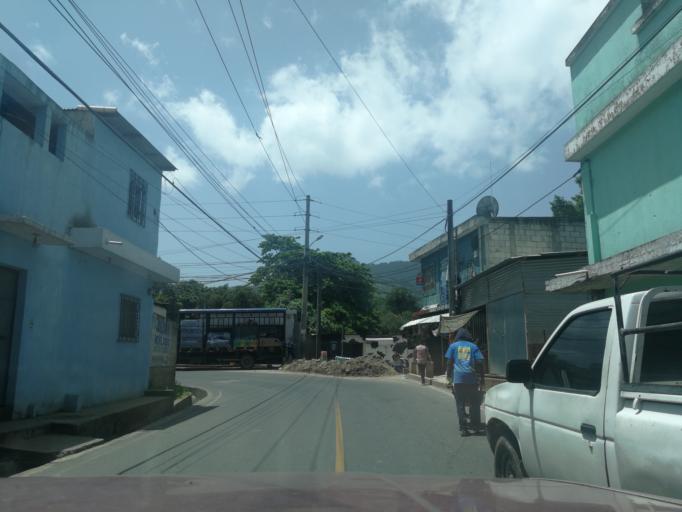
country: GT
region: Guatemala
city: Santa Catarina Pinula
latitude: 14.5443
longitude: -90.5159
